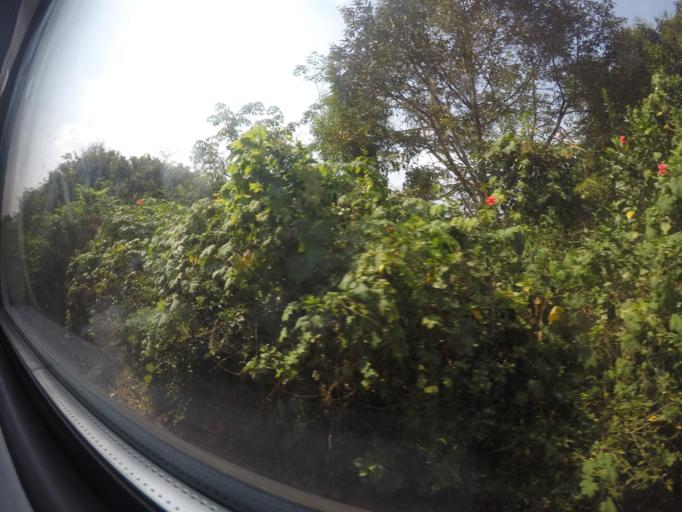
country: VN
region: Dong Nai
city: Long Khanh
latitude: 10.9310
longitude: 107.2200
